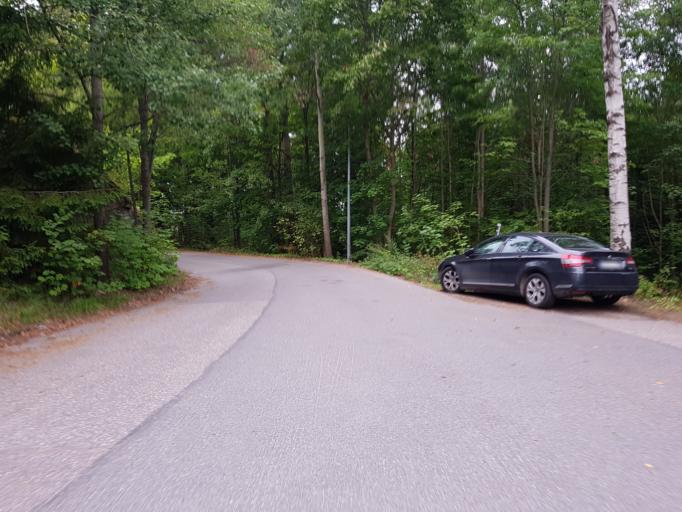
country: FI
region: Uusimaa
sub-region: Helsinki
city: Helsinki
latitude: 60.2300
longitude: 24.9799
